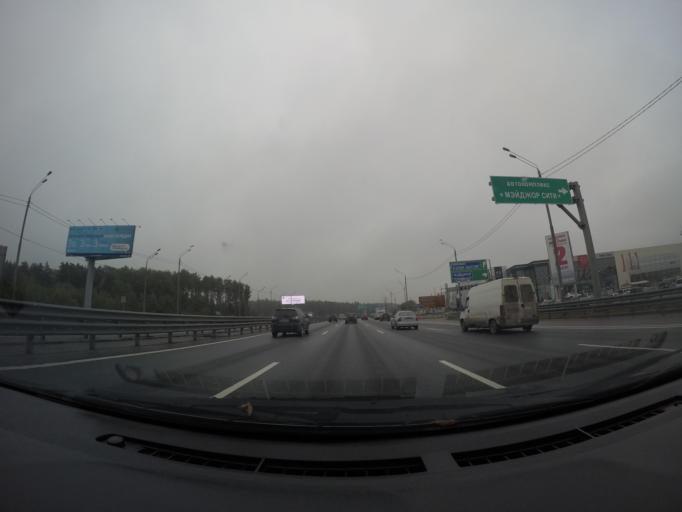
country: RU
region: Moskovskaya
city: Opalikha
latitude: 55.7907
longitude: 37.2597
